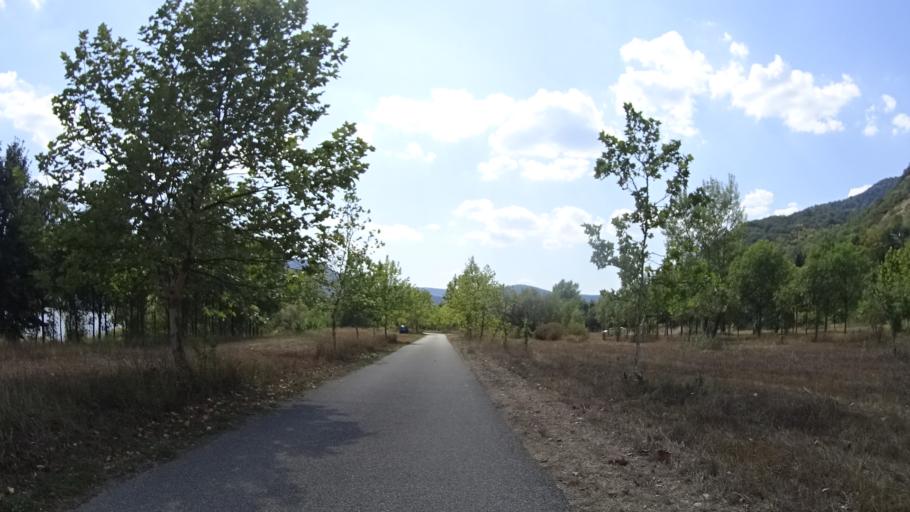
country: HU
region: Pest
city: Nagymaros
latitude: 47.7712
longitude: 18.9454
